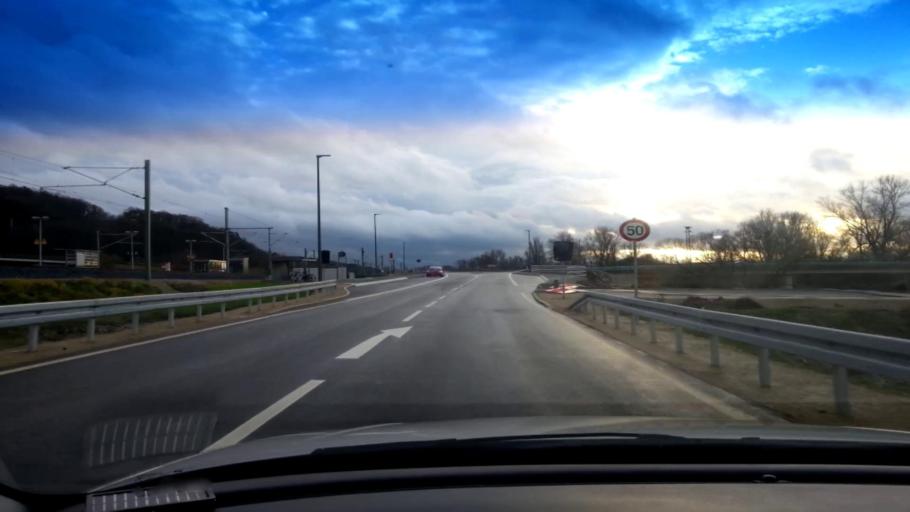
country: DE
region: Bavaria
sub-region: Upper Franconia
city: Zapfendorf
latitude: 50.0026
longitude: 10.9146
